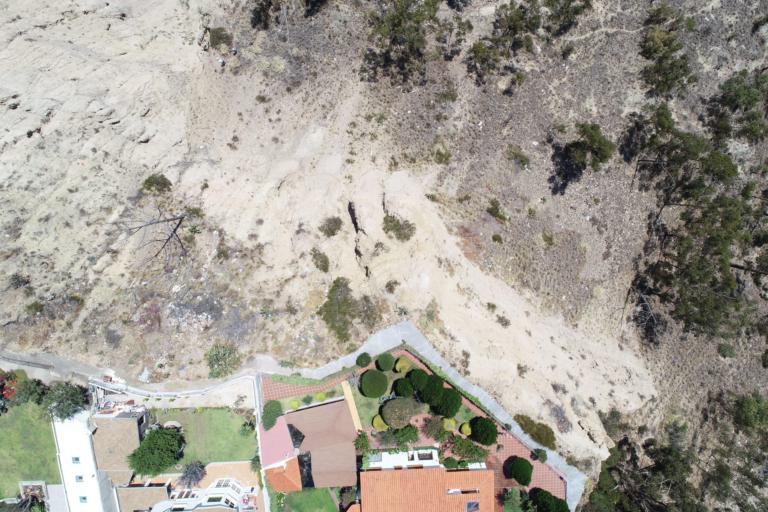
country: BO
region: La Paz
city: La Paz
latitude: -16.5298
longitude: -68.0909
